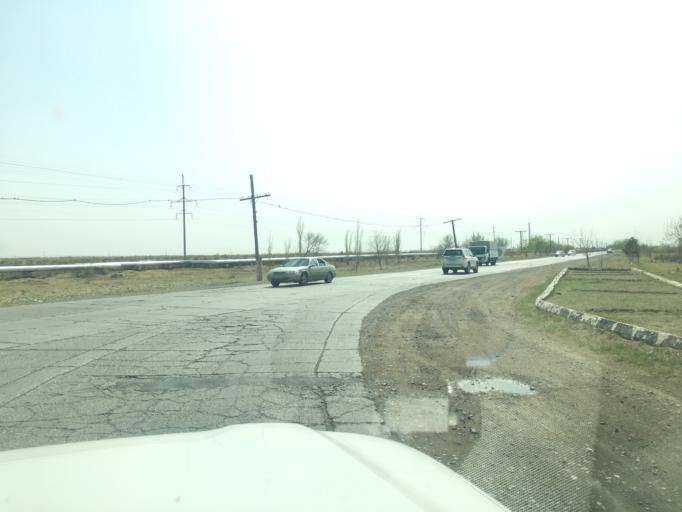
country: TM
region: Mary
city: Seydi
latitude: 39.4539
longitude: 62.8906
